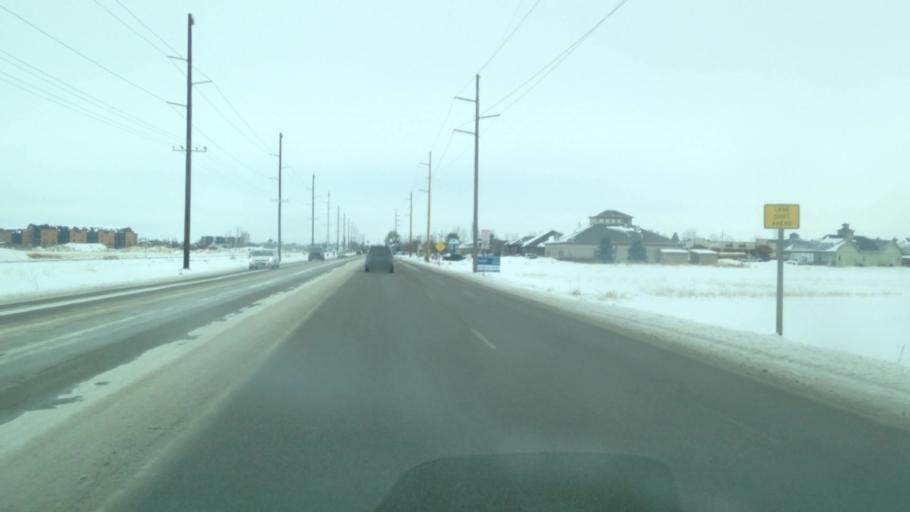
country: US
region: Idaho
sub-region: Madison County
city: Rexburg
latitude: 43.8051
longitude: -111.8078
